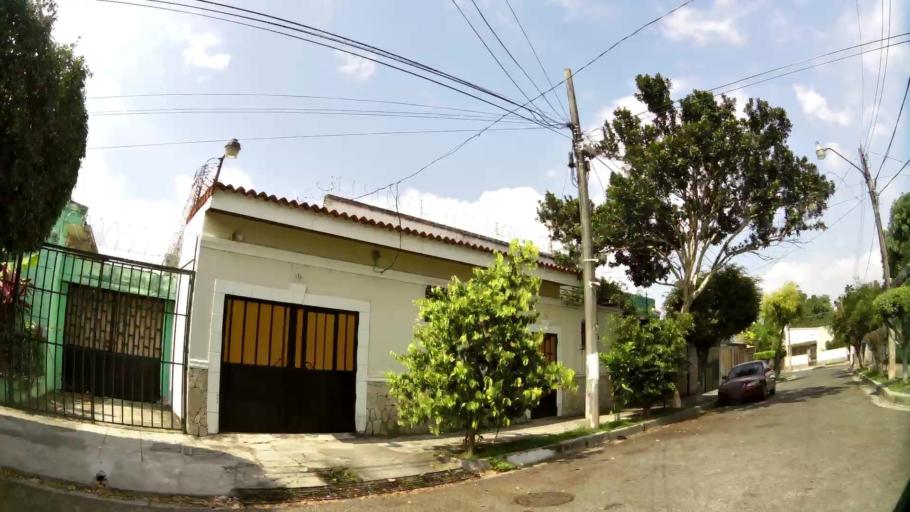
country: SV
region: San Salvador
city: Mejicanos
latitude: 13.7142
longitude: -89.2123
